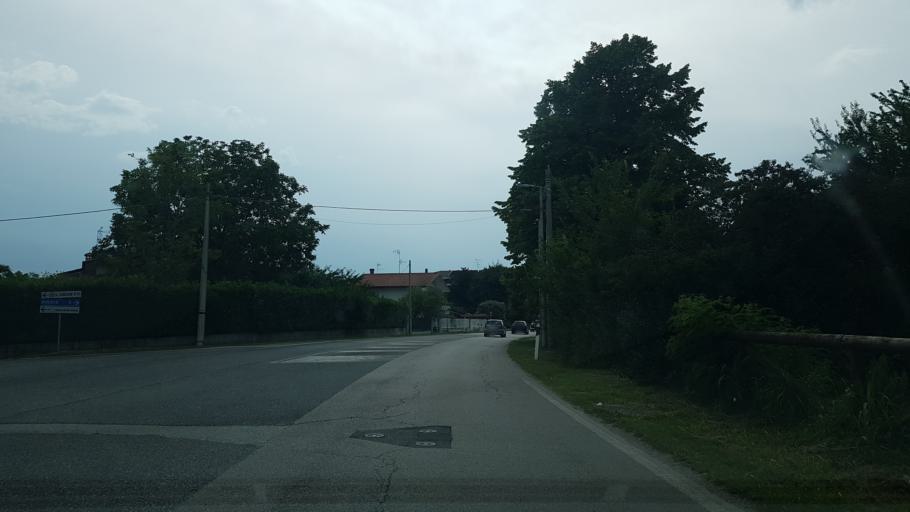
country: IT
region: Friuli Venezia Giulia
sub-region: Provincia di Gorizia
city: San Canzian d'Isonzo
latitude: 45.7999
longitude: 13.4708
